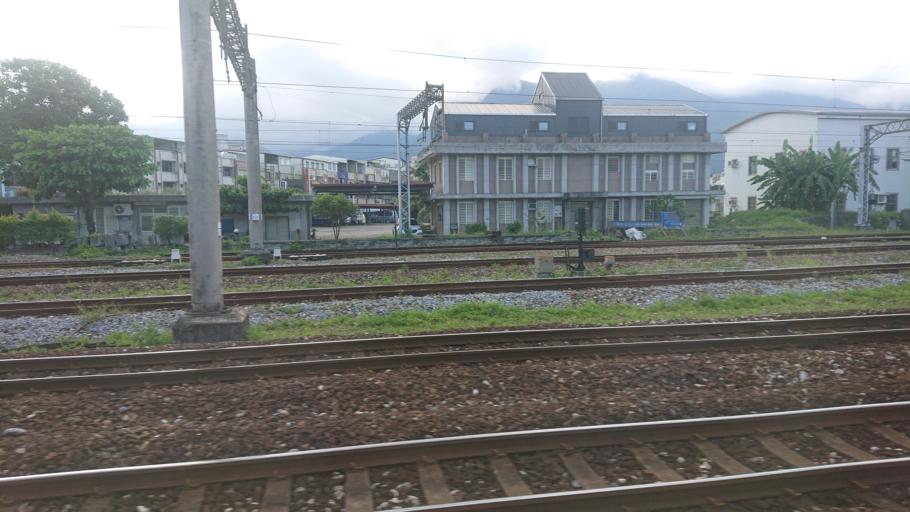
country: TW
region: Taiwan
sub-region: Hualien
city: Hualian
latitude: 23.9903
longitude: 121.5997
